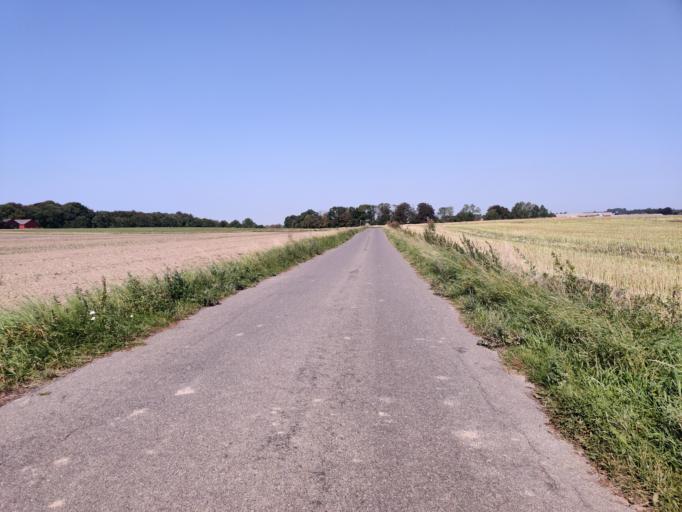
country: DK
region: Zealand
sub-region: Guldborgsund Kommune
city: Nykobing Falster
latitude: 54.6837
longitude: 11.8917
